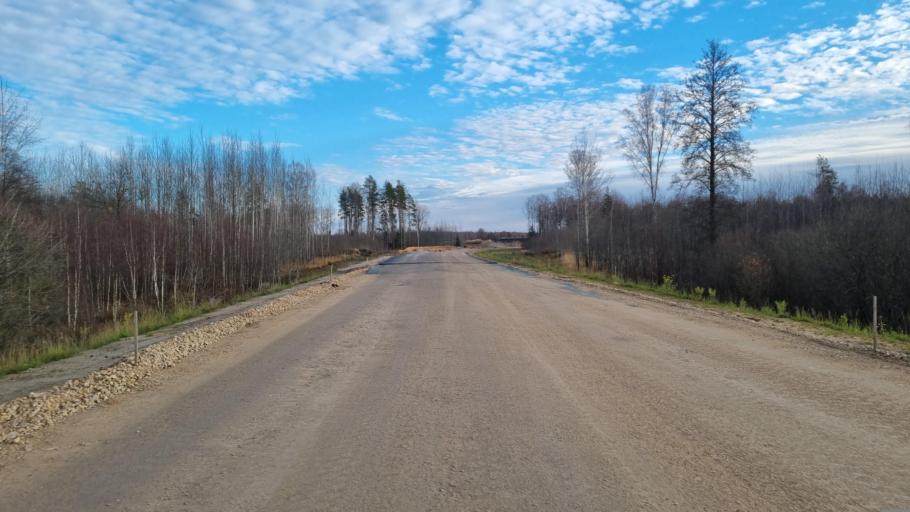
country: LV
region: Kekava
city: Kekava
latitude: 56.7829
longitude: 24.2326
